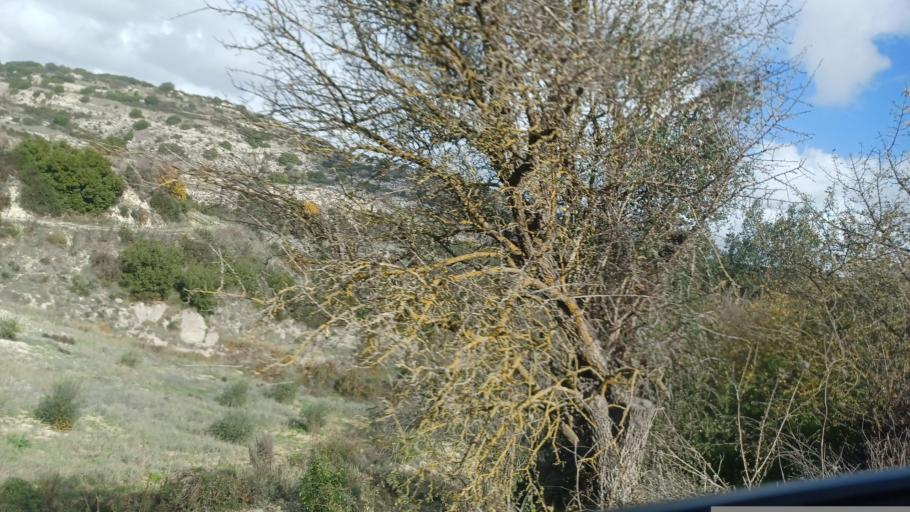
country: CY
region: Pafos
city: Mesogi
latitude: 34.8739
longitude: 32.5250
